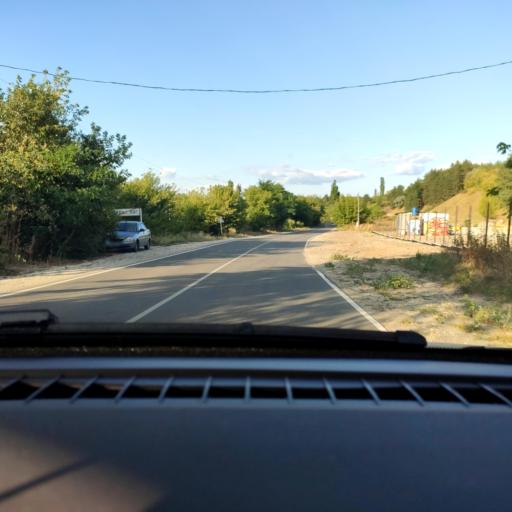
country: RU
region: Voronezj
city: Semiluki
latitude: 51.6662
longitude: 39.0161
